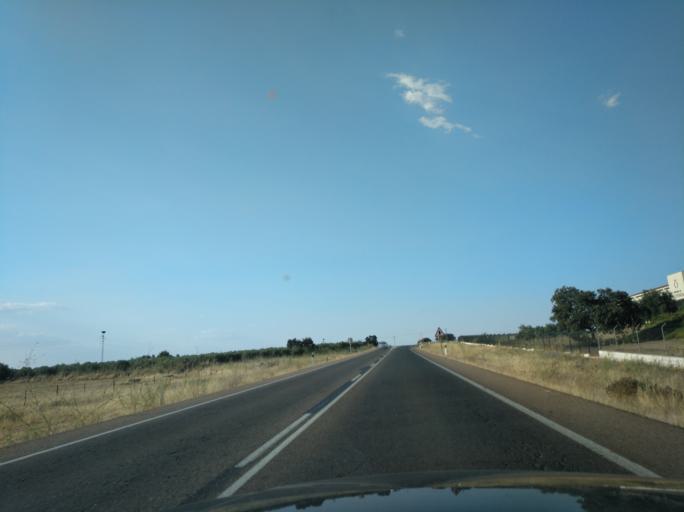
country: ES
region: Extremadura
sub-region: Provincia de Badajoz
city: Olivenza
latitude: 38.7086
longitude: -7.0863
